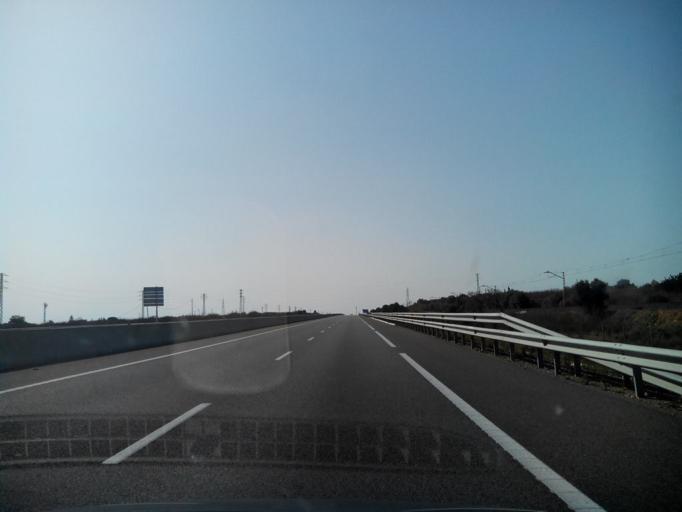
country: ES
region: Catalonia
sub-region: Provincia de Tarragona
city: Alcover
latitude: 41.2358
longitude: 1.1646
